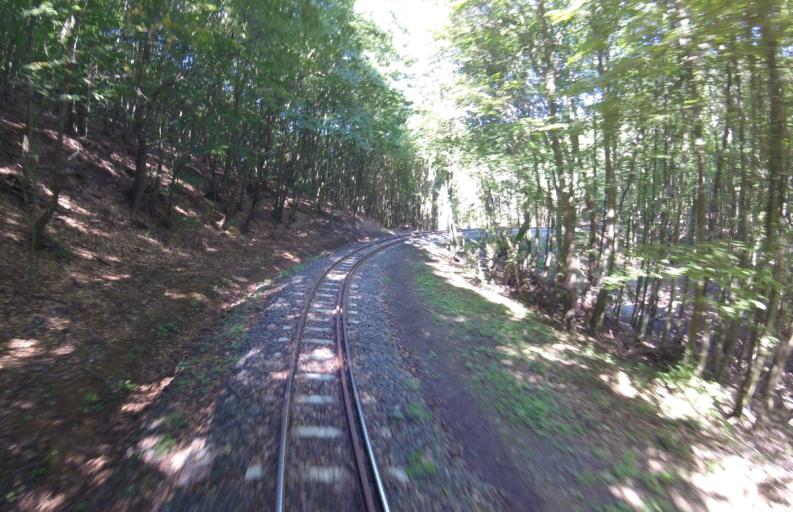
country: HU
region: Pest
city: Szob
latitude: 47.8925
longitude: 18.8799
